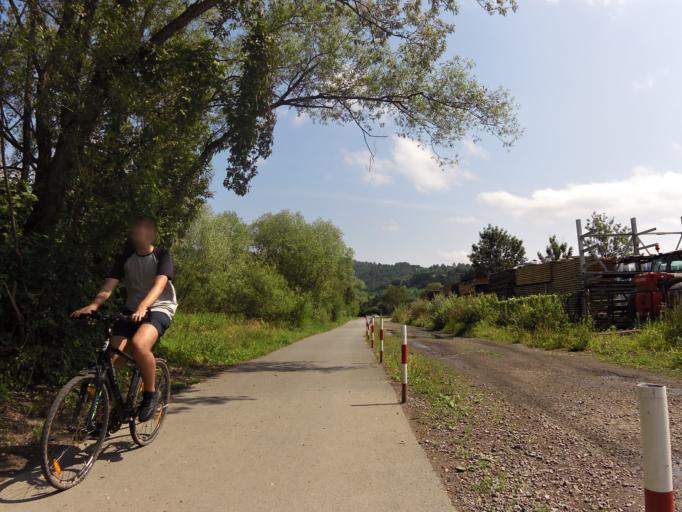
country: PL
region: Silesian Voivodeship
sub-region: Powiat zywiecki
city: Rajcza
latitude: 49.5075
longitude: 19.1051
